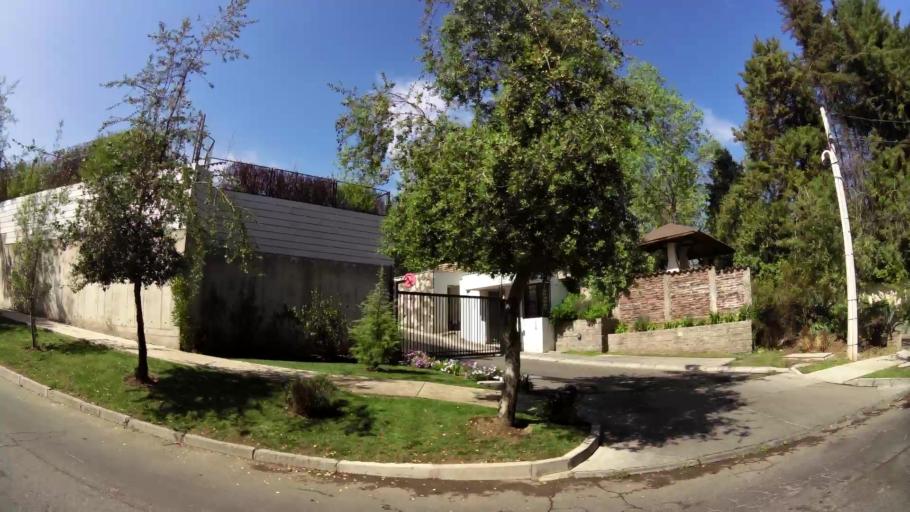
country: CL
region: Santiago Metropolitan
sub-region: Provincia de Santiago
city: Villa Presidente Frei, Nunoa, Santiago, Chile
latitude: -33.4435
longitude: -70.5232
